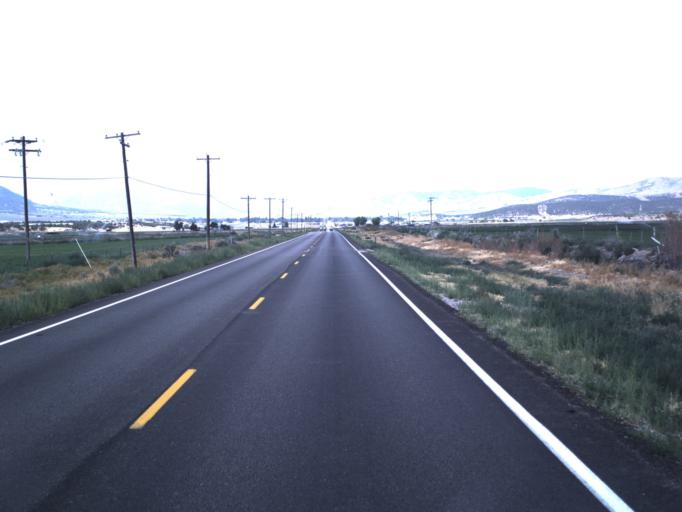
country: US
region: Utah
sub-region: Sanpete County
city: Fountain Green
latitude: 39.5878
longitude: -111.6155
